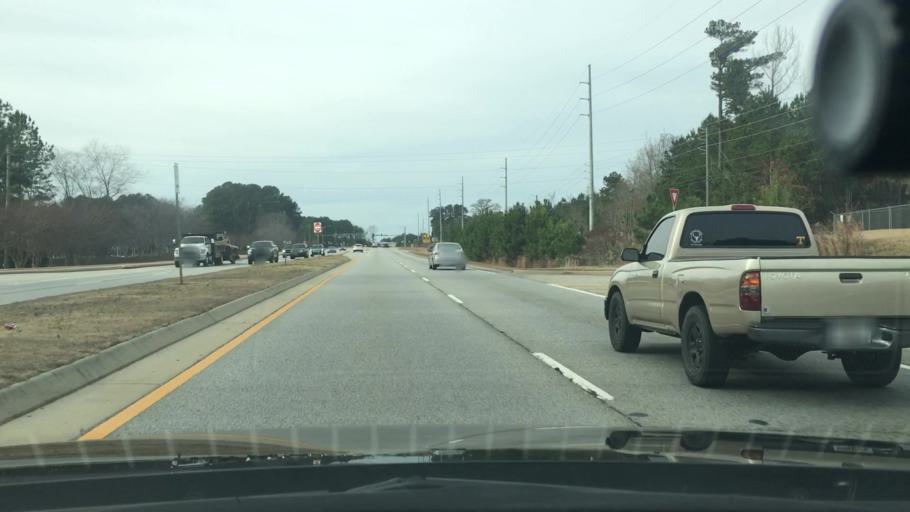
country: US
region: Georgia
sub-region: Coweta County
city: Senoia
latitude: 33.3512
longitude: -84.5527
